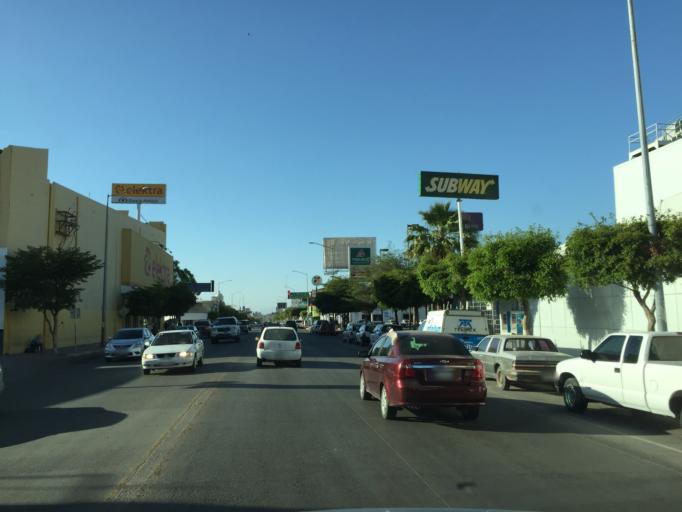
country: MX
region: Sonora
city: Navojoa
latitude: 27.0795
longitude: -109.4446
